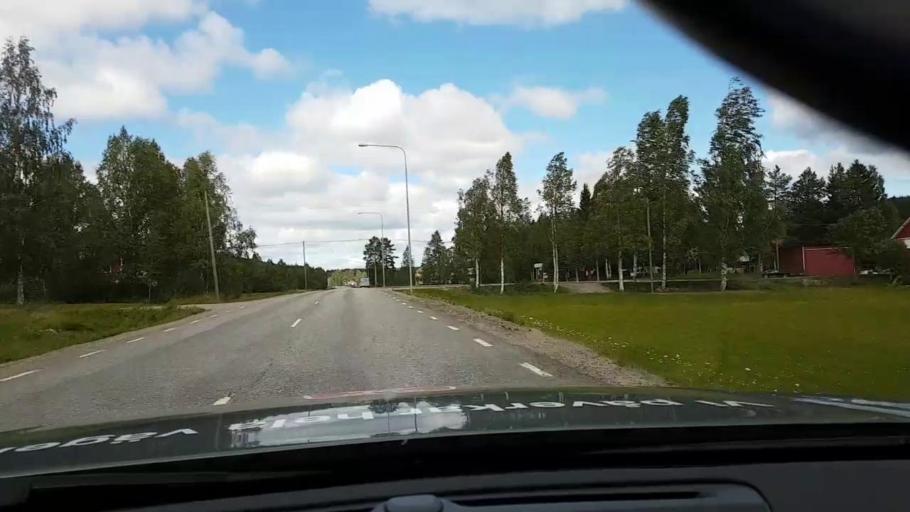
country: SE
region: Vaesternorrland
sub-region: OErnskoeldsviks Kommun
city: Bredbyn
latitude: 63.4759
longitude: 18.0952
